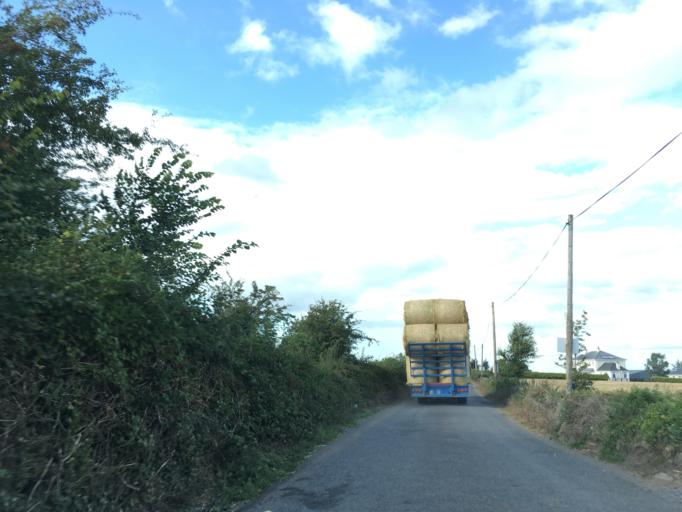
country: IE
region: Munster
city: Cahir
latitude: 52.2991
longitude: -7.9474
